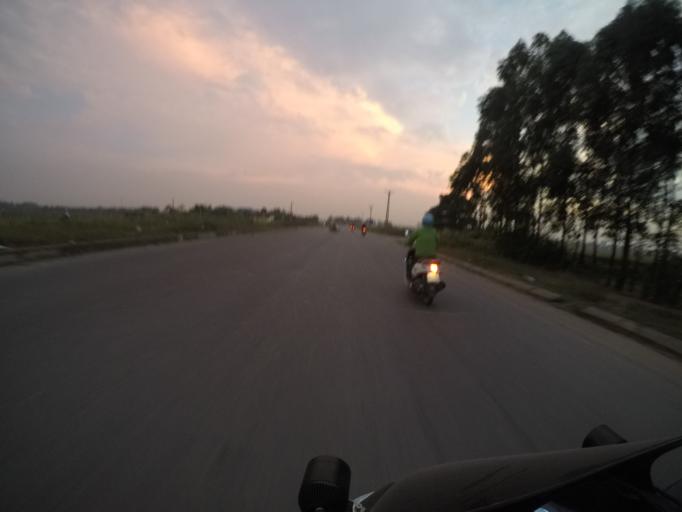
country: VN
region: Vinh Phuc
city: Phuc Yen
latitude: 21.2555
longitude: 105.7224
